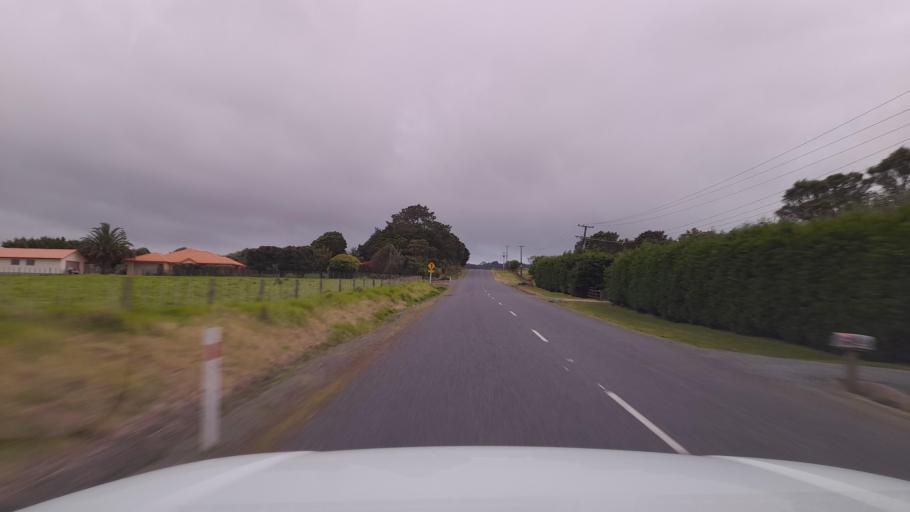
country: NZ
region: Northland
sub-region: Whangarei
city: Maungatapere
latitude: -35.6627
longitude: 174.2283
